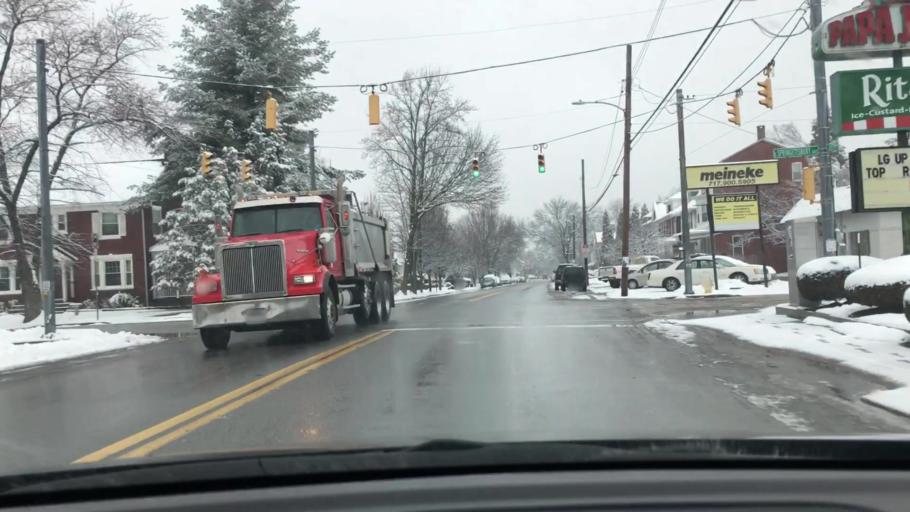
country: US
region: Pennsylvania
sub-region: York County
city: Valley View
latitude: 39.9519
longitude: -76.7162
